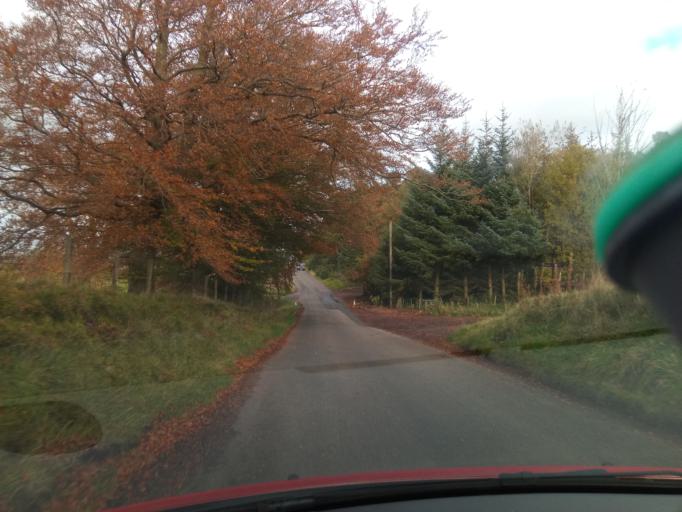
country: GB
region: Scotland
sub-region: South Lanarkshire
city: Carnwath
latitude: 55.7453
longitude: -3.6053
